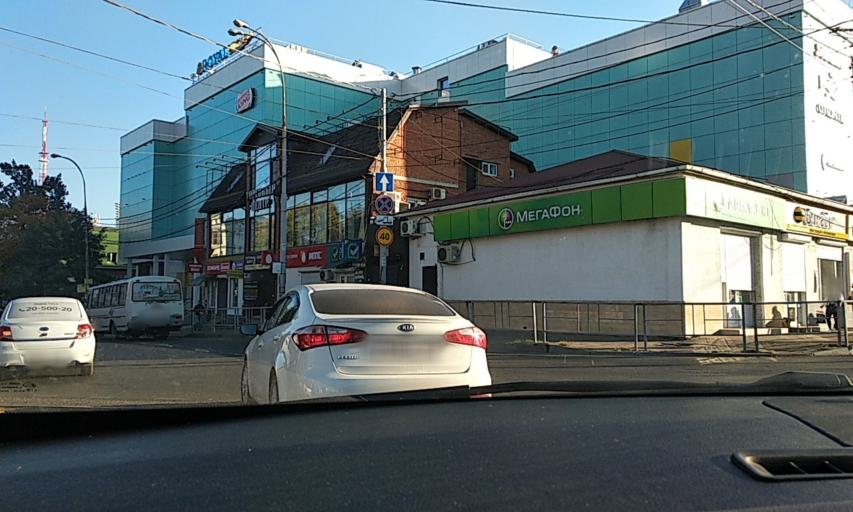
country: RU
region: Krasnodarskiy
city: Krasnodar
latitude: 45.0199
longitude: 38.9996
